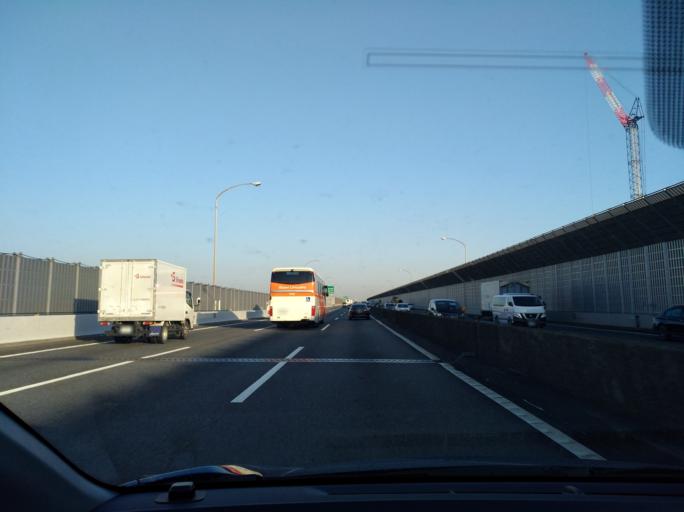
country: JP
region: Chiba
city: Funabashi
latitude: 35.6830
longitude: 139.9910
